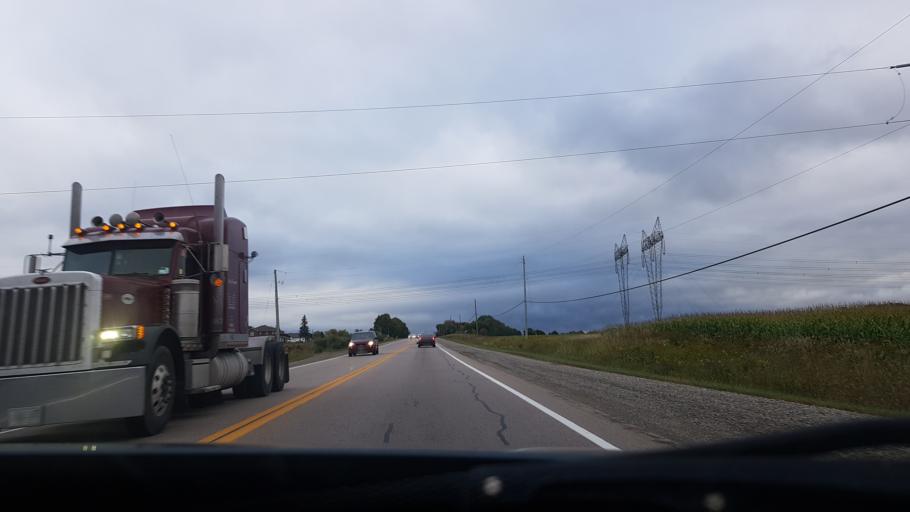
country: CA
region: Ontario
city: Bradford West Gwillimbury
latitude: 44.0038
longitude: -79.7117
